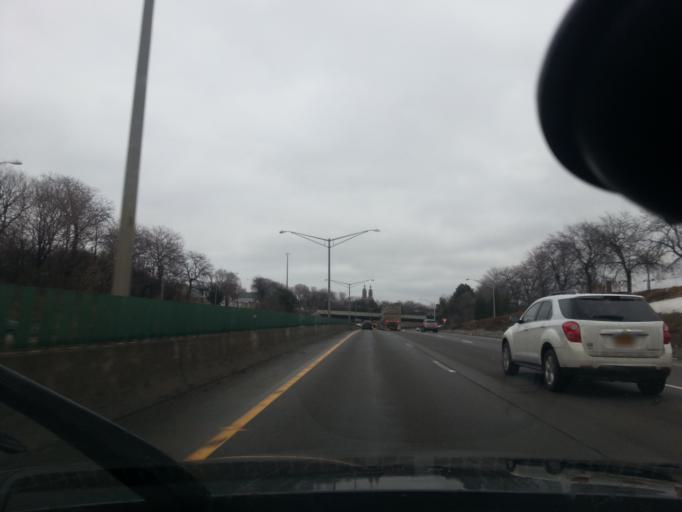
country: US
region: New York
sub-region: Onondaga County
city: Syracuse
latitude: 43.0662
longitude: -76.1635
